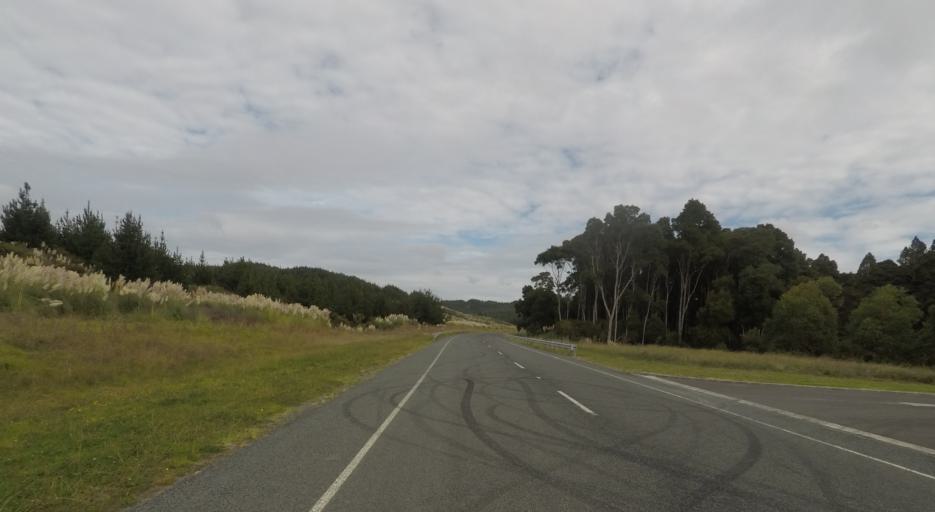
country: NZ
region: Auckland
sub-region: Auckland
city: Rothesay Bay
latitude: -36.6530
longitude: 174.7177
